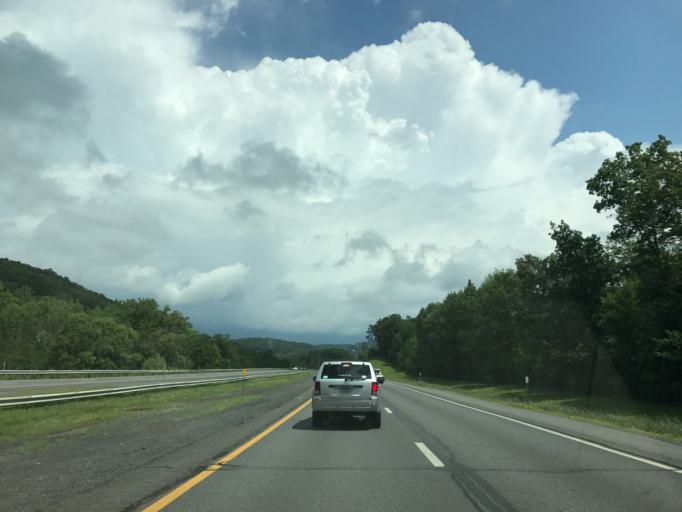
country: US
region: New York
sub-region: Greene County
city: Coxsackie
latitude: 42.3705
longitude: -73.8434
